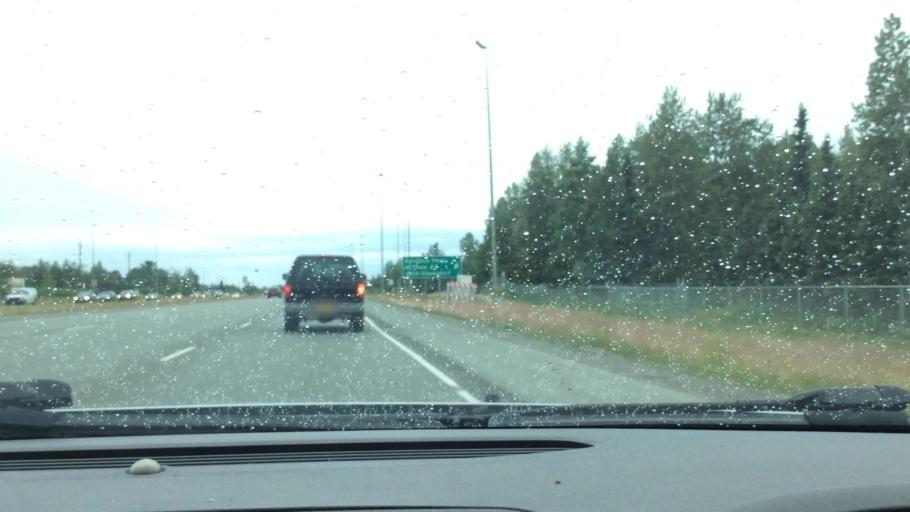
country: US
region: Alaska
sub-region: Anchorage Municipality
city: Anchorage
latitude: 61.2247
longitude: -149.7664
